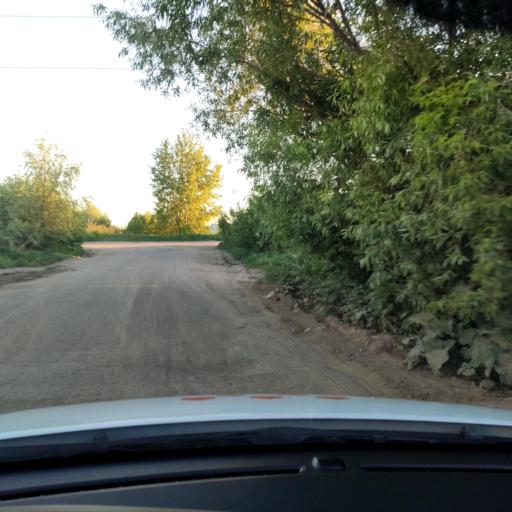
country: RU
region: Tatarstan
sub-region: Gorod Kazan'
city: Kazan
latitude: 55.7223
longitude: 49.1281
